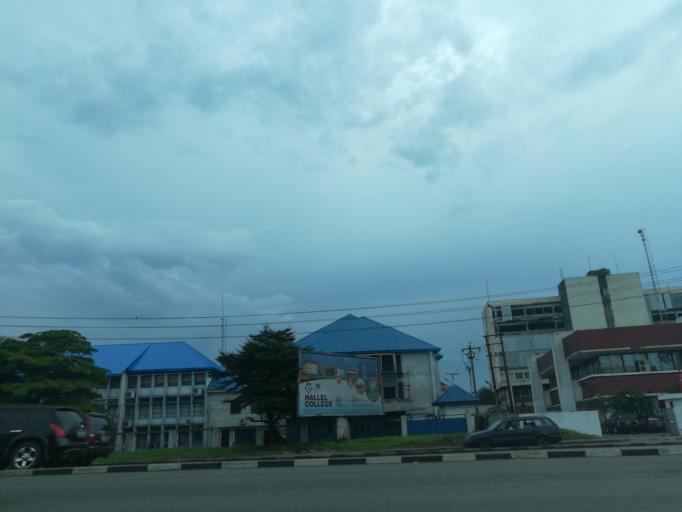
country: NG
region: Rivers
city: Port Harcourt
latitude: 4.7856
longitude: 7.0050
